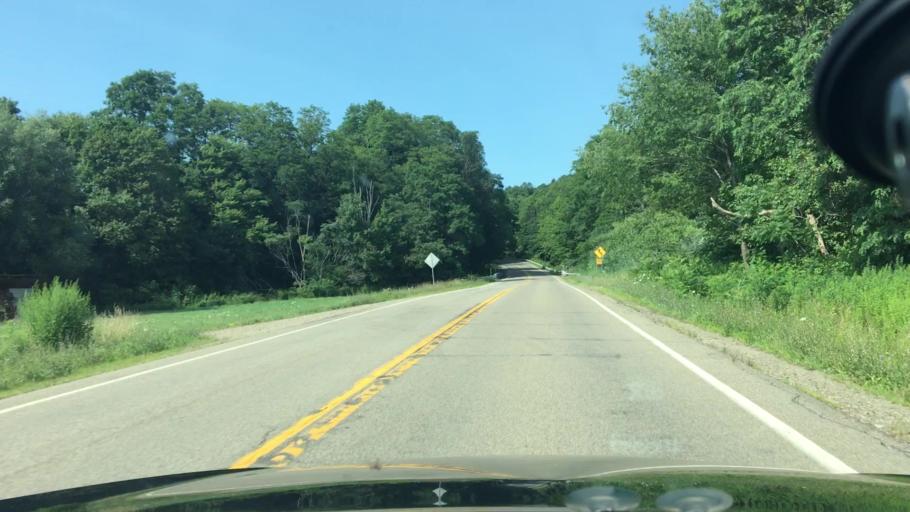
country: US
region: New York
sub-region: Chautauqua County
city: Brocton
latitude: 42.3386
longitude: -79.3661
